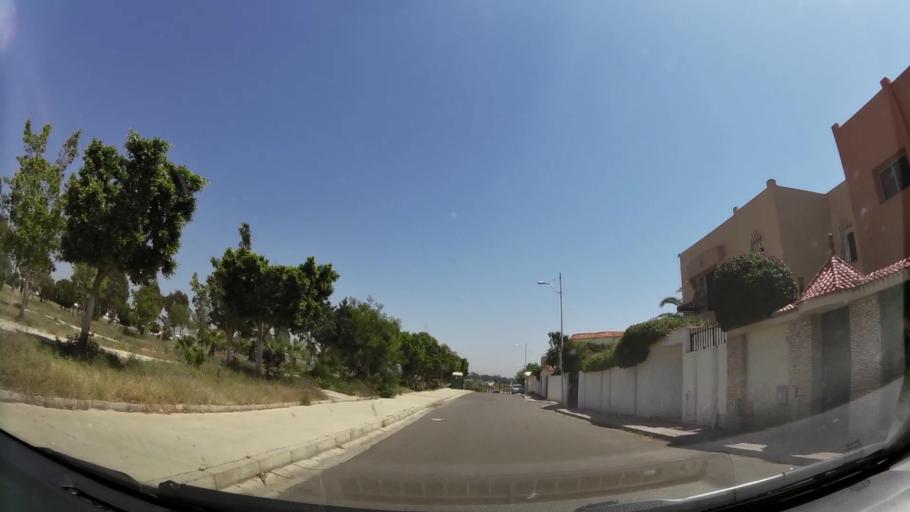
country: MA
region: Souss-Massa-Draa
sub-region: Agadir-Ida-ou-Tnan
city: Agadir
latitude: 30.4362
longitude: -9.5822
